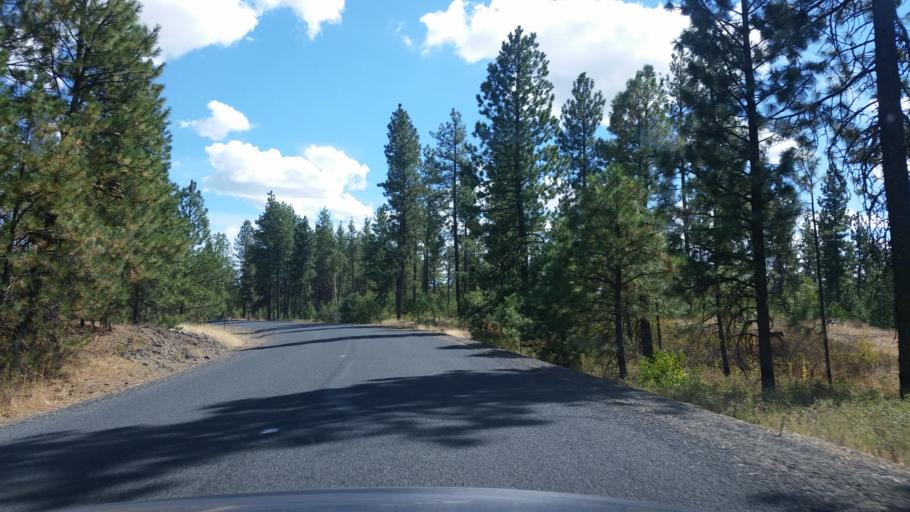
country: US
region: Washington
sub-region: Spokane County
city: Medical Lake
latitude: 47.5015
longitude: -117.6652
